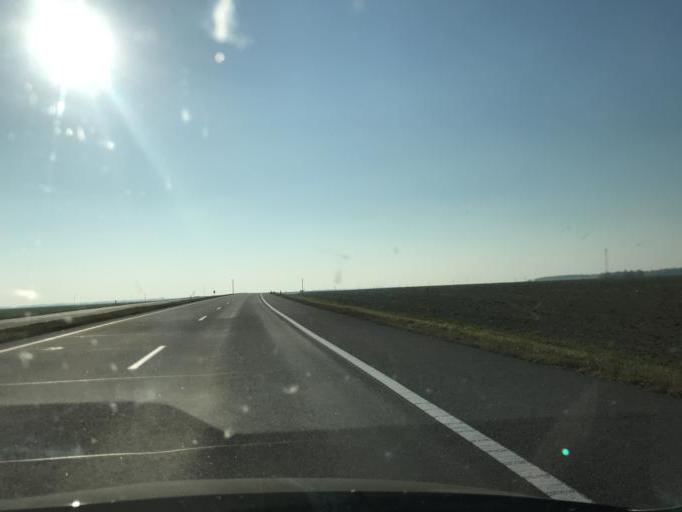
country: BY
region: Minsk
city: Haradzyeya
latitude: 53.4131
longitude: 26.5670
